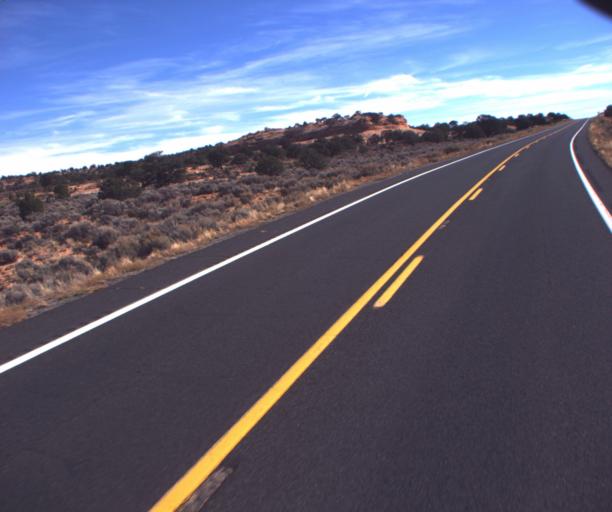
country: US
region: Arizona
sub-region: Coconino County
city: Kaibito
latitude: 36.5634
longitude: -110.7360
